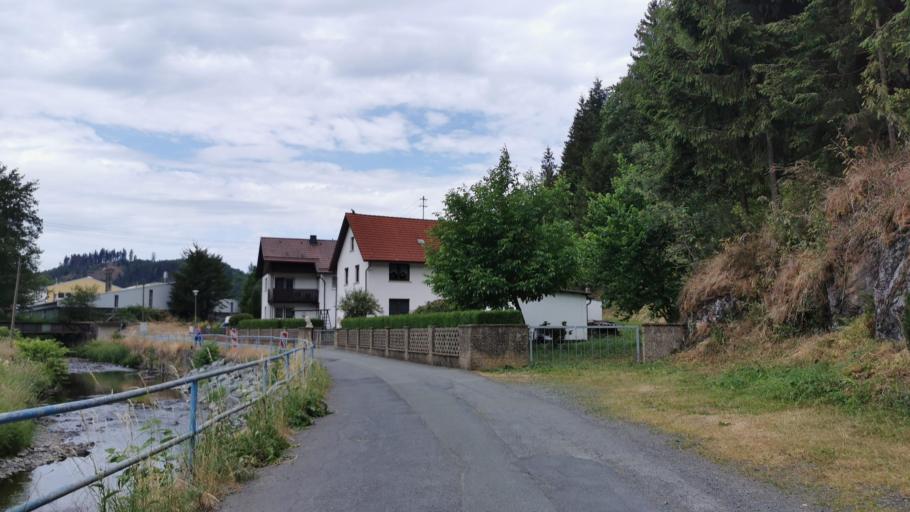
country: DE
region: Bavaria
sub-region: Upper Franconia
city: Steinwiesen
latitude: 50.2899
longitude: 11.4552
